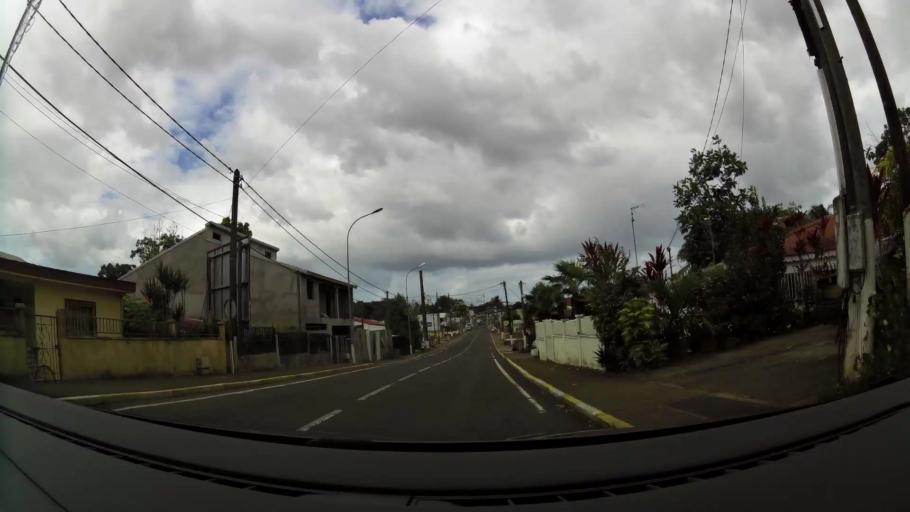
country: GP
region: Guadeloupe
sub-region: Guadeloupe
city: Lamentin
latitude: 16.2682
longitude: -61.6311
